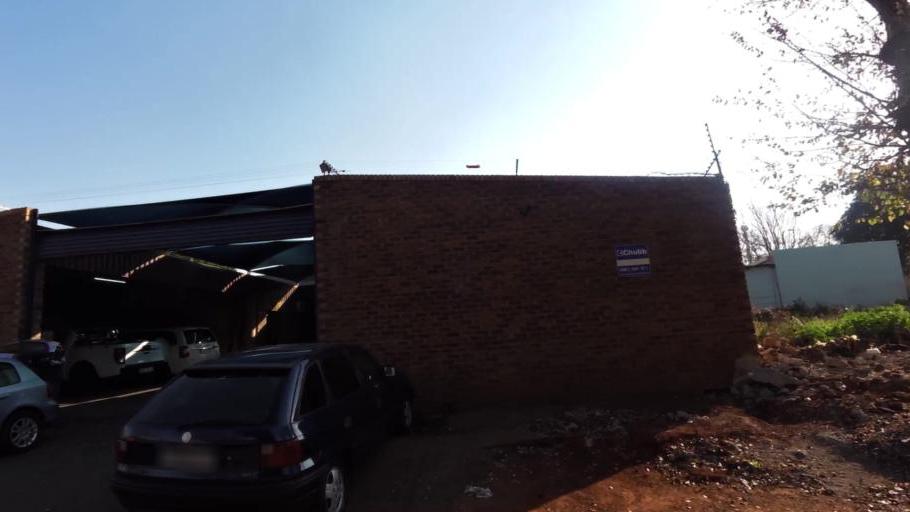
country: ZA
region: Gauteng
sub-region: City of Johannesburg Metropolitan Municipality
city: Johannesburg
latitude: -26.1968
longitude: 28.0194
